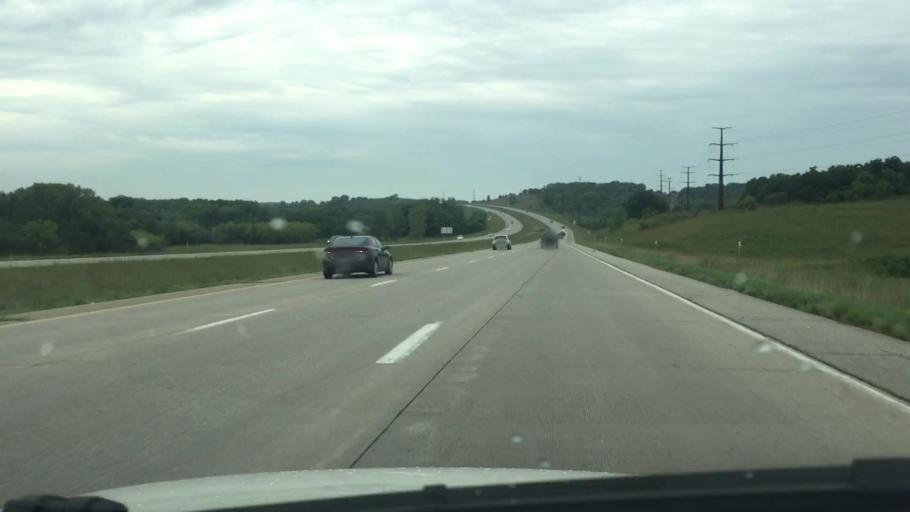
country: US
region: Iowa
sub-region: Warren County
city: Carlisle
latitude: 41.5049
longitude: -93.5810
